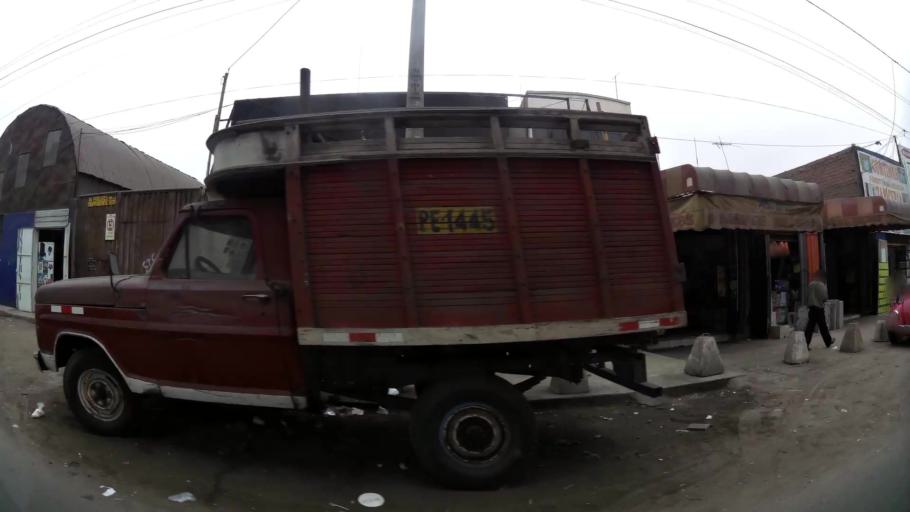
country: PE
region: Lima
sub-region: Lima
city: Independencia
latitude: -11.9806
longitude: -77.0051
